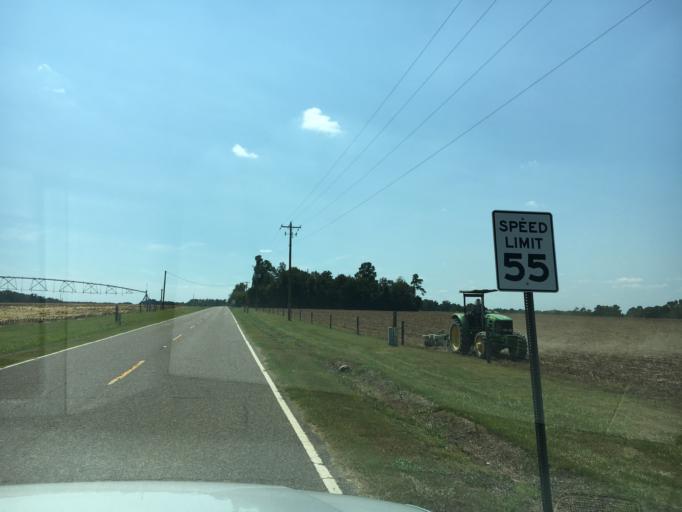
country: US
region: South Carolina
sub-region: Lexington County
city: Batesburg
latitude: 33.8392
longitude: -81.6623
